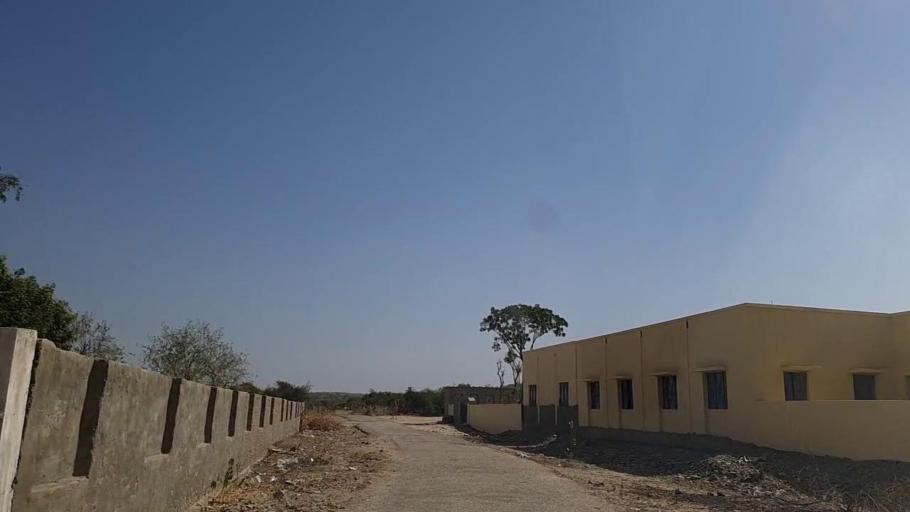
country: PK
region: Sindh
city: Mithi
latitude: 24.7035
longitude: 69.5945
